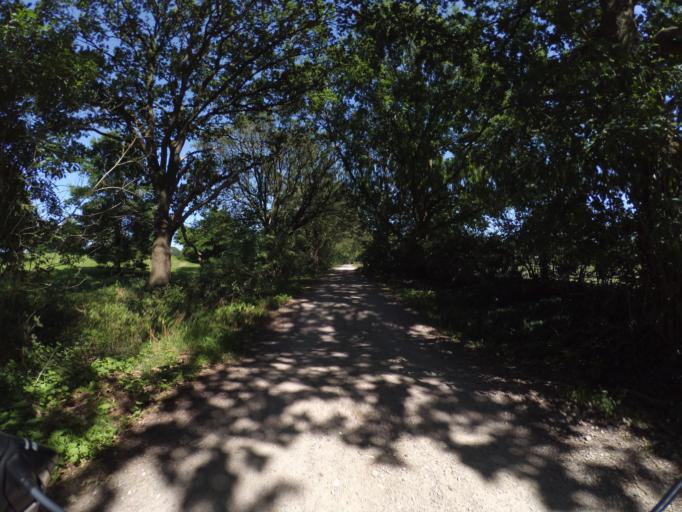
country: NL
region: North Brabant
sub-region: Gemeente Loon op Zand
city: Loon op Zand
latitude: 51.6470
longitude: 5.0347
